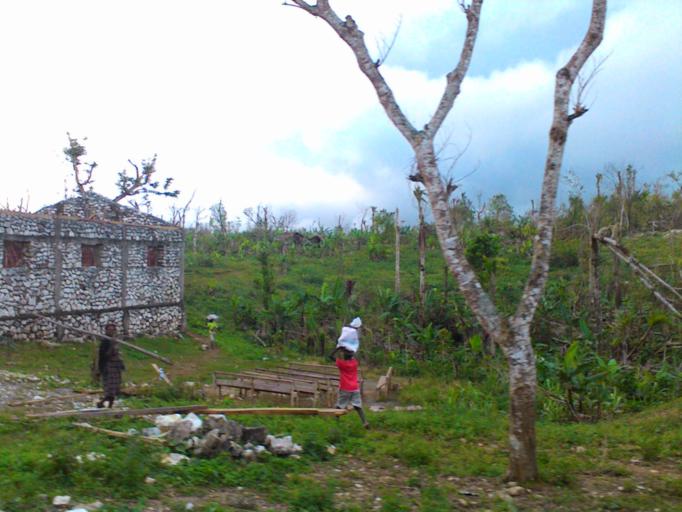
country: HT
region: Grandans
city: Jeremie
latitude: 18.4890
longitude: -74.1108
